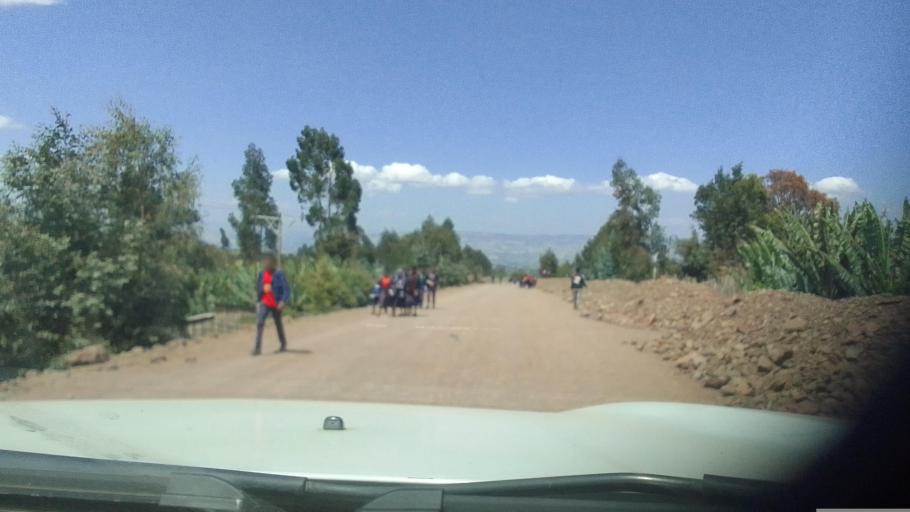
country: ET
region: Oromiya
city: Hagere Hiywet
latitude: 8.8587
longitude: 37.8914
